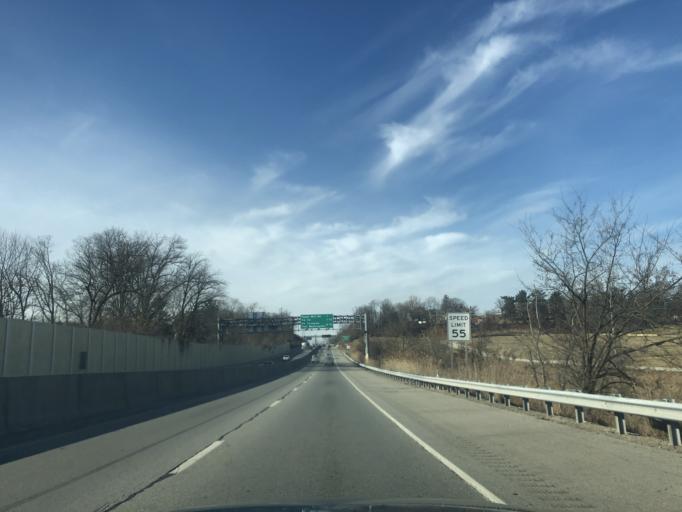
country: US
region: Pennsylvania
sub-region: Montgomery County
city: Wyndmoor
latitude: 40.0948
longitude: -75.1727
